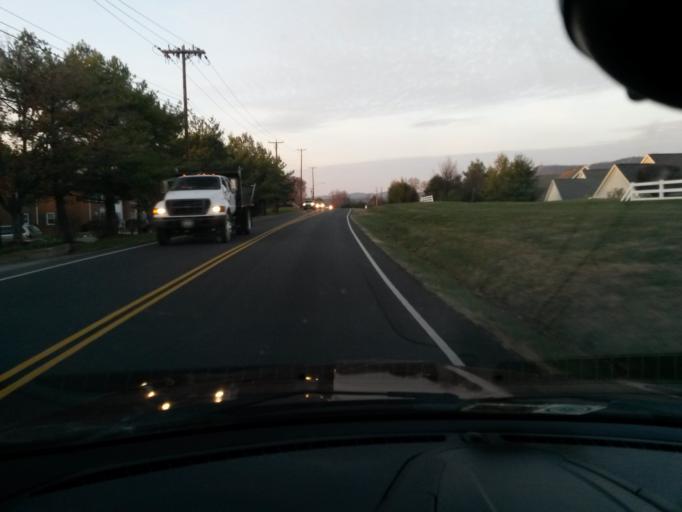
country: US
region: Virginia
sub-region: Roanoke County
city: Hollins
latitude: 37.3356
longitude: -79.9410
